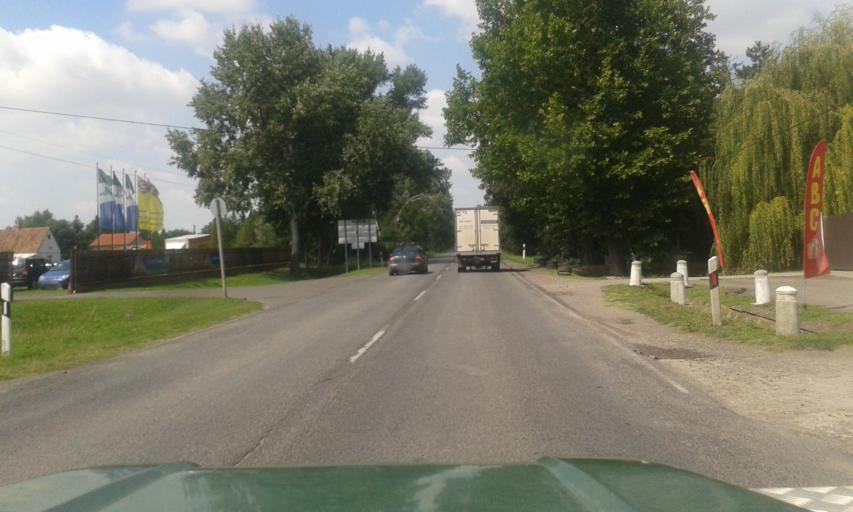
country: HU
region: Csongrad
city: Szatymaz
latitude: 46.3505
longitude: 20.0586
